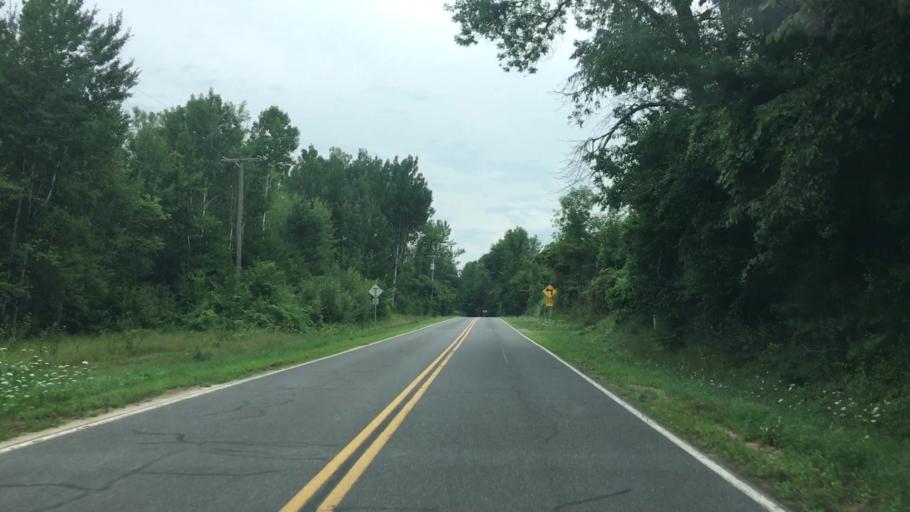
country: US
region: New York
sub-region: Clinton County
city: Peru
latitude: 44.5283
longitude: -73.5737
